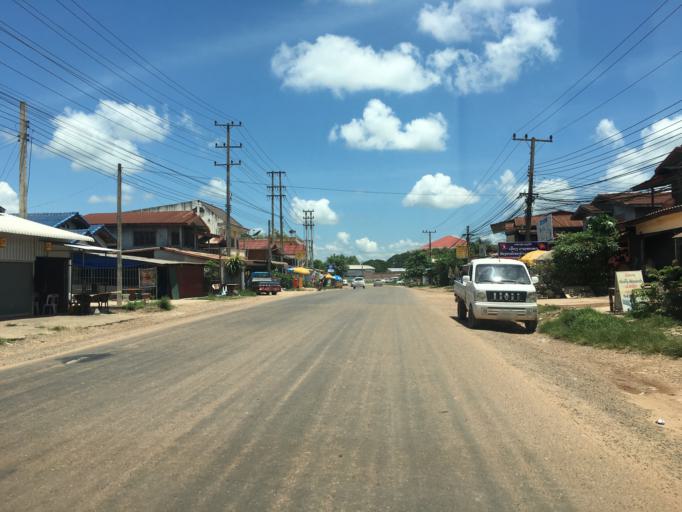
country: LA
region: Vientiane
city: Vientiane
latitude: 18.0482
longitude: 102.5455
